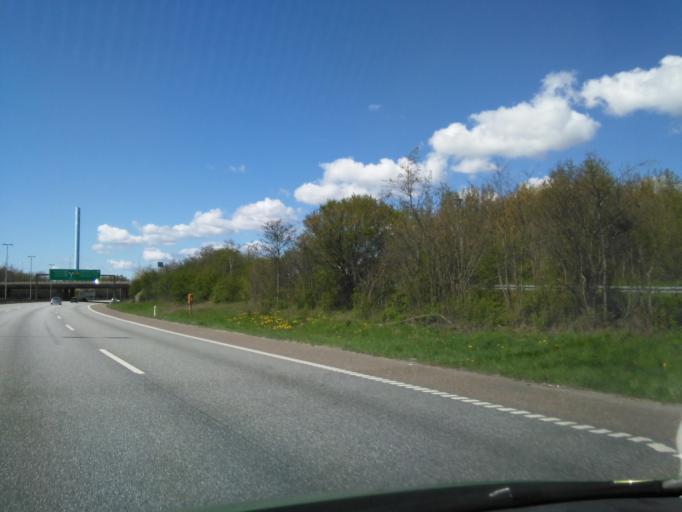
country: DK
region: Capital Region
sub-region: Hvidovre Kommune
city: Hvidovre
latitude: 55.6167
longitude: 12.4490
